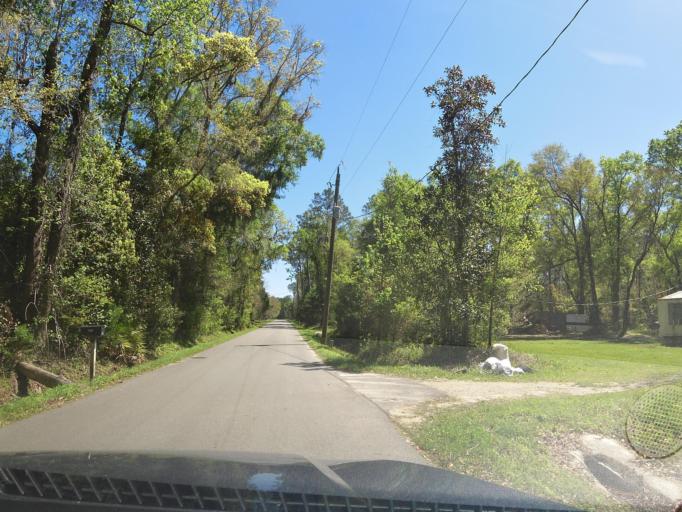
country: US
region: Florida
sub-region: Bradford County
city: Starke
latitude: 30.0491
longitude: -82.0686
